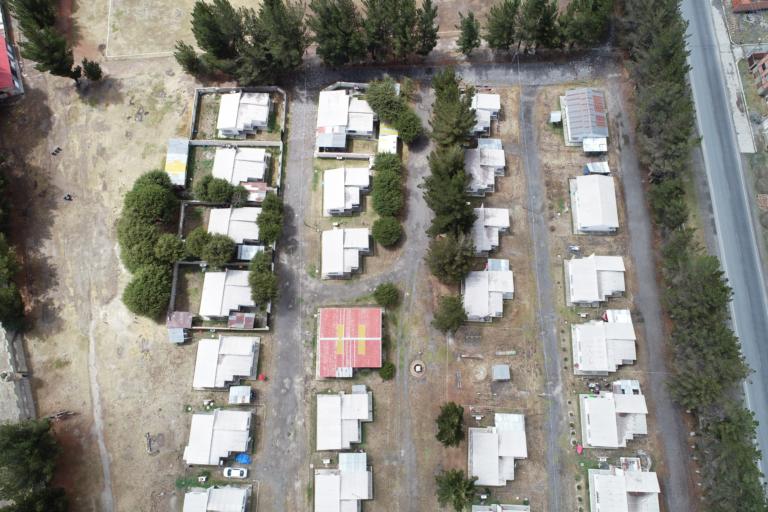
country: BO
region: La Paz
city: Achacachi
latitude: -16.0317
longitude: -68.6879
